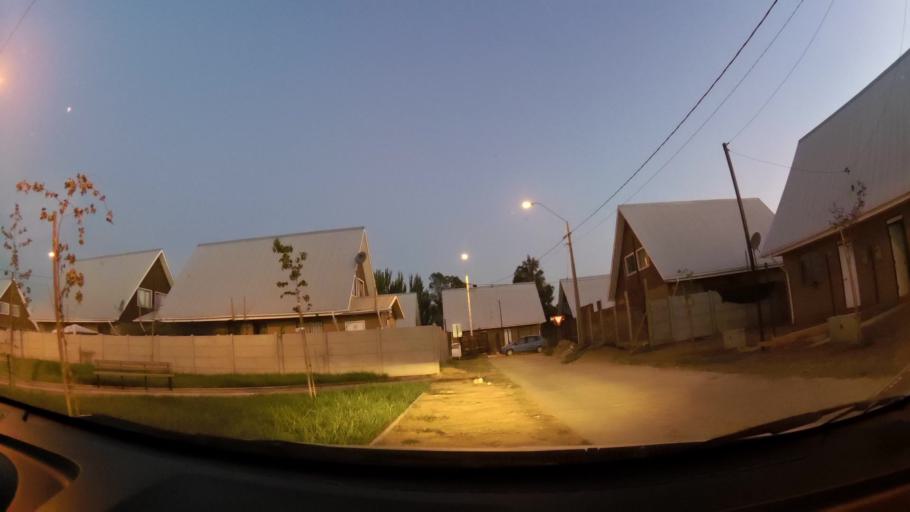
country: CL
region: Maule
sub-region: Provincia de Talca
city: Talca
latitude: -35.4415
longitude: -71.6215
